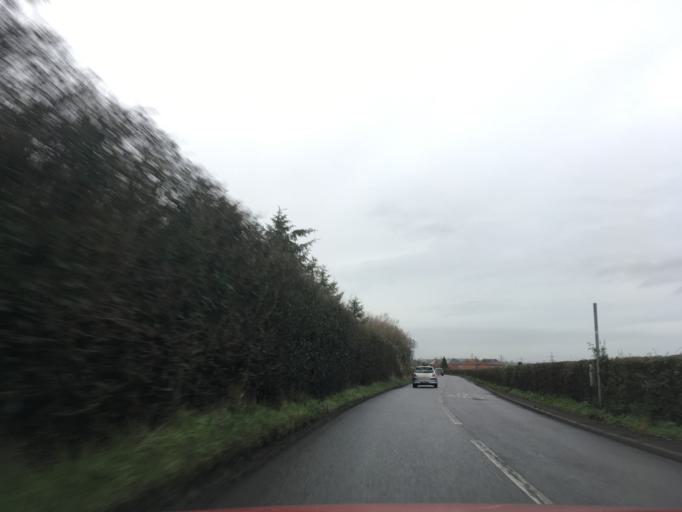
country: GB
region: Wales
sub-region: Newport
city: Nash
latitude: 51.5525
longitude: -2.9420
